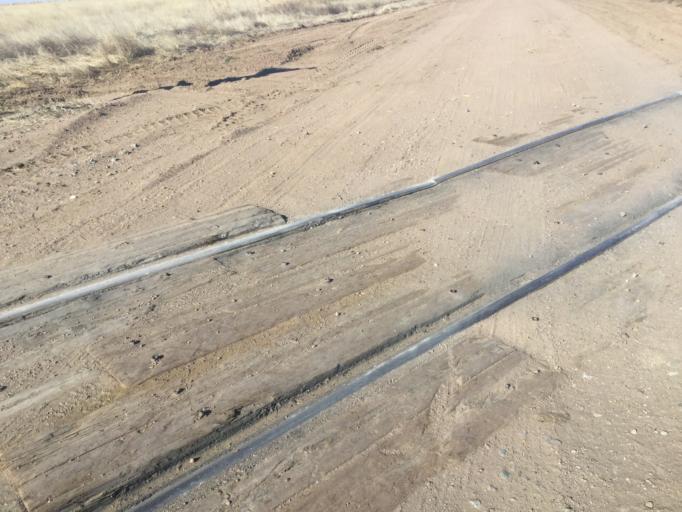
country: US
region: Kansas
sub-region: Haskell County
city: Satanta
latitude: 37.5039
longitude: -101.1200
